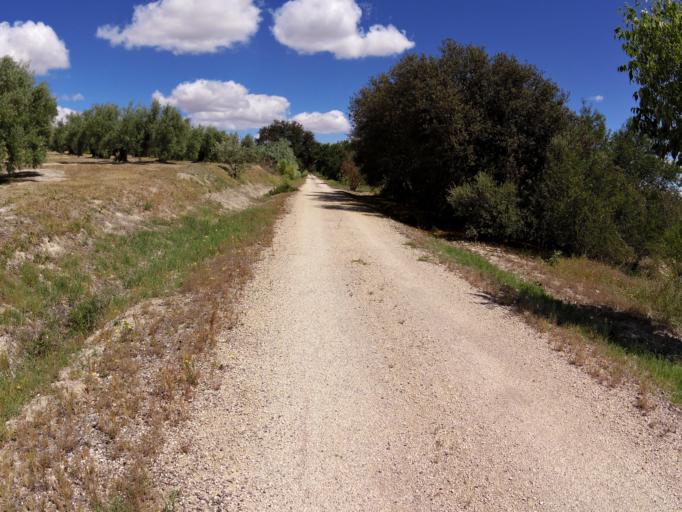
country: ES
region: Andalusia
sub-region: Provincia de Jaen
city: Alcaudete
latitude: 37.6578
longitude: -4.0623
